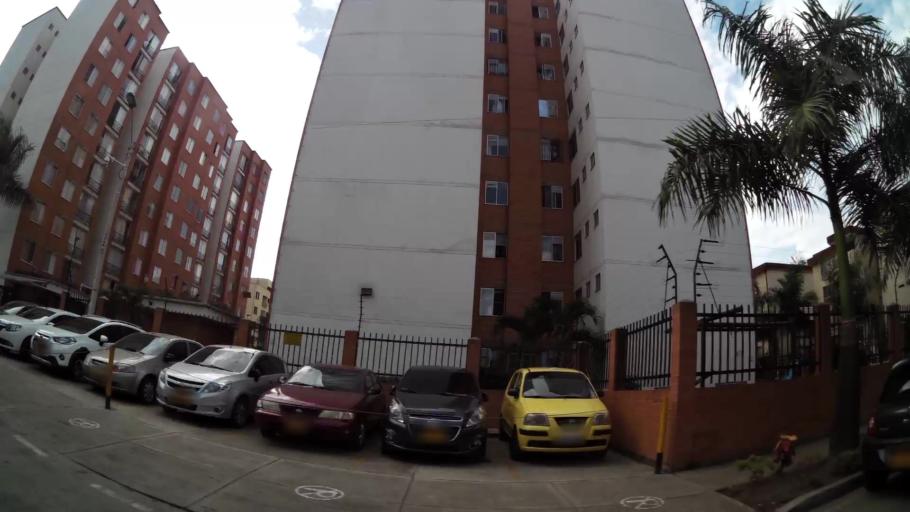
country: CO
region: Valle del Cauca
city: Cali
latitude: 3.4684
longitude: -76.5201
